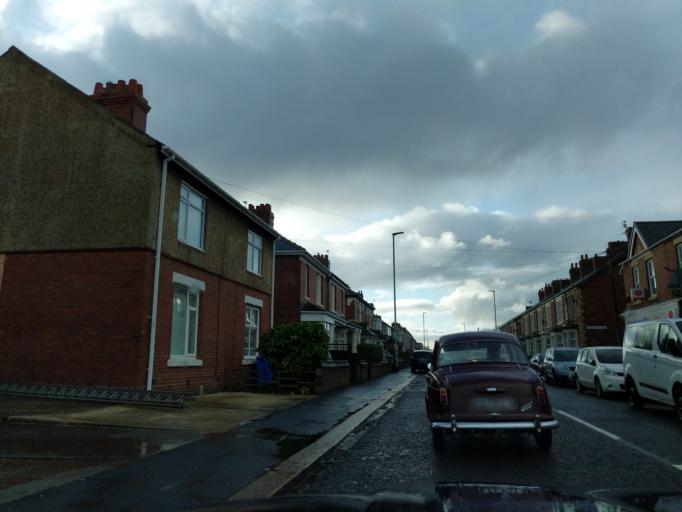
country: GB
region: England
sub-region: Northumberland
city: Blyth
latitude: 55.1212
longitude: -1.5087
